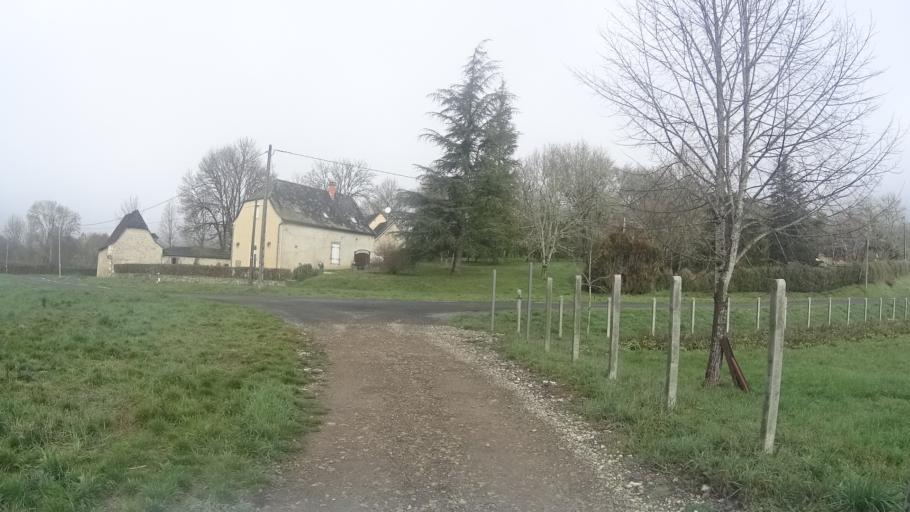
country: FR
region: Aquitaine
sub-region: Departement de la Dordogne
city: Terrasson-Lavilledieu
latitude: 45.1027
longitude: 1.2661
